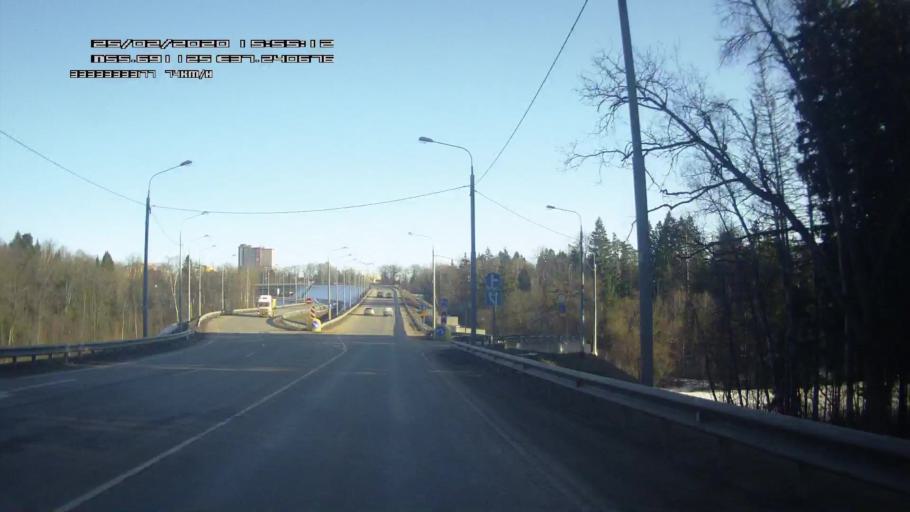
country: RU
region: Moskovskaya
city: Odintsovo
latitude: 55.6916
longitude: 37.2401
